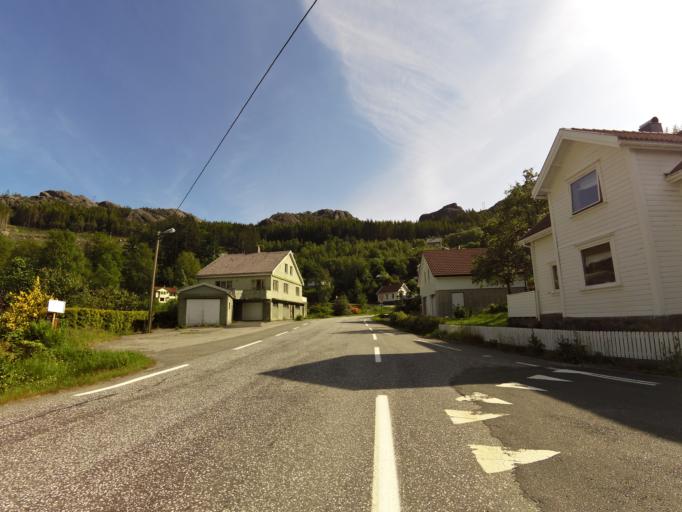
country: NO
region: Rogaland
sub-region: Sokndal
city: Hauge i Dalane
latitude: 58.3168
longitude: 6.3451
